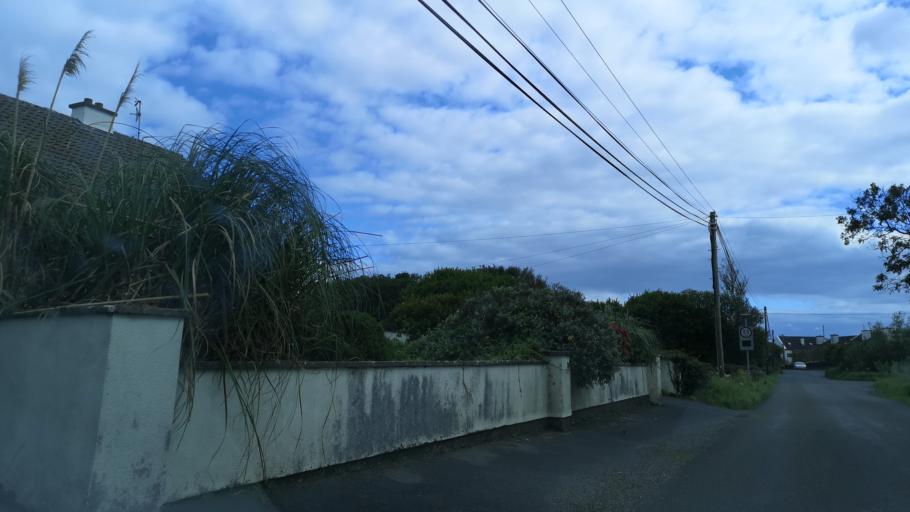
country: IE
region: Connaught
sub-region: County Galway
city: Bearna
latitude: 53.2540
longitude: -9.1533
